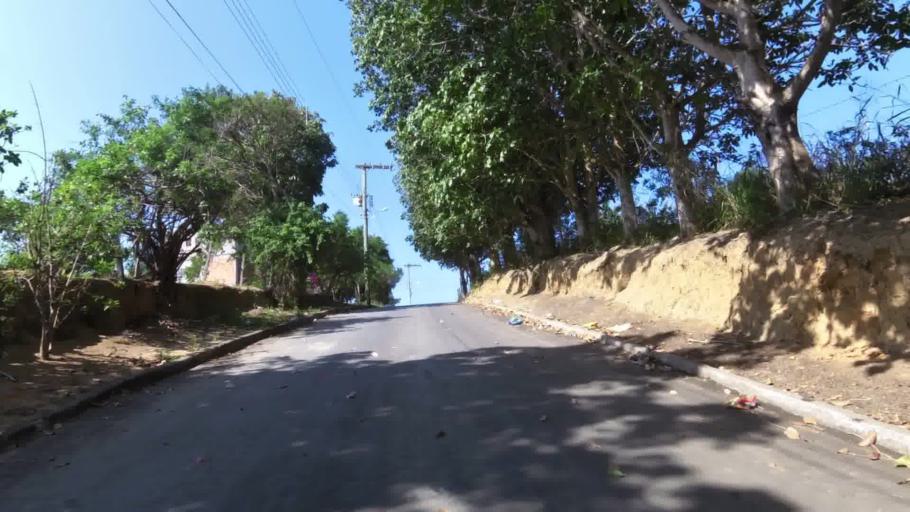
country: BR
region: Espirito Santo
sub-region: Marataizes
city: Marataizes
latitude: -21.0351
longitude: -40.8244
